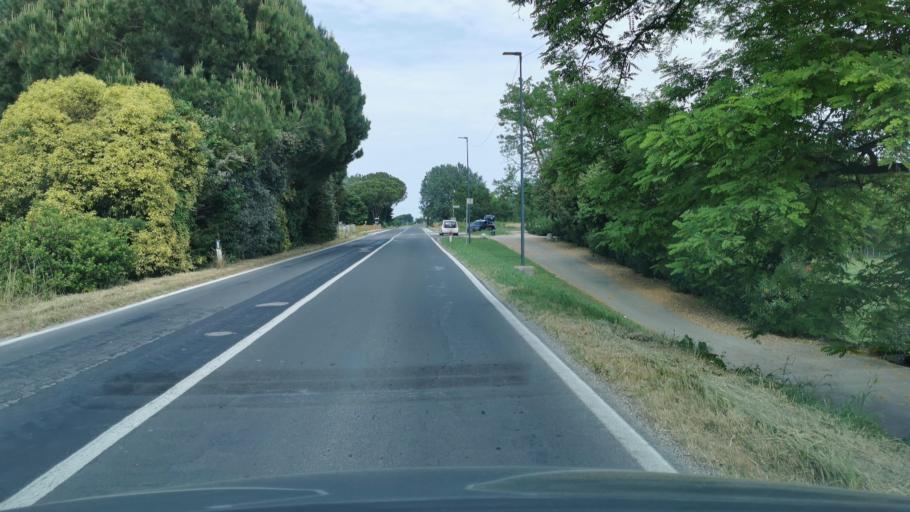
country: IT
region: Emilia-Romagna
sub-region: Provincia di Ravenna
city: Savarna-Conventella
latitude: 44.5353
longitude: 12.1264
